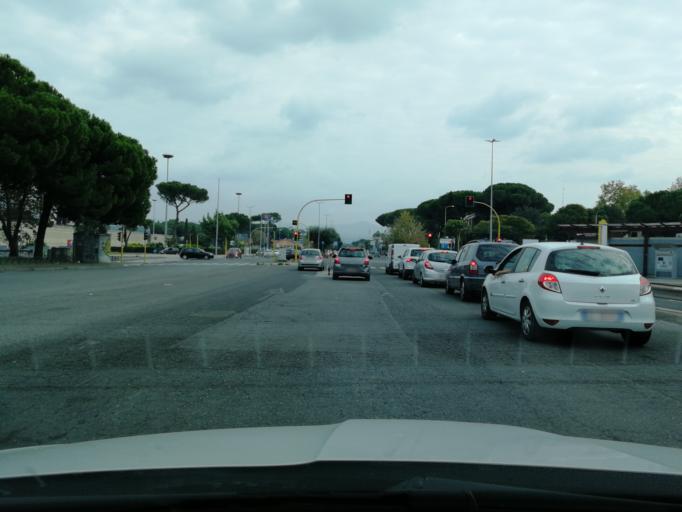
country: IT
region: Latium
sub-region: Citta metropolitana di Roma Capitale
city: Ciampino
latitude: 41.8529
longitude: 12.5690
